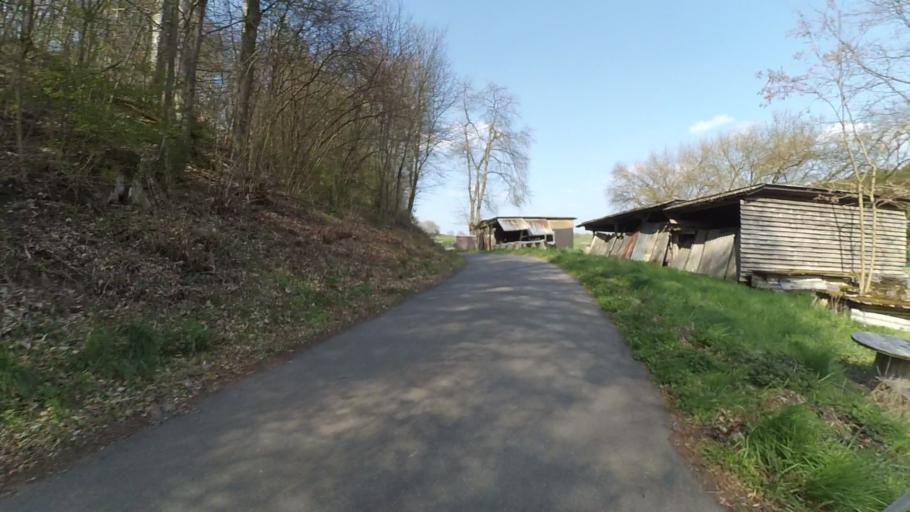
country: DE
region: Rheinland-Pfalz
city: Weidenhahn
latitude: 50.5536
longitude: 7.8215
